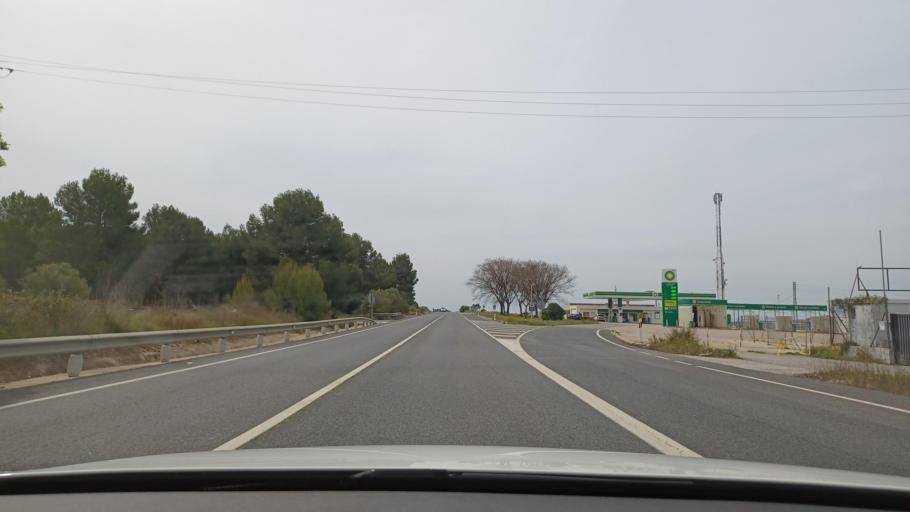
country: ES
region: Catalonia
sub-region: Provincia de Tarragona
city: la Pobla de Mafumet
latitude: 41.1751
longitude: 1.2402
